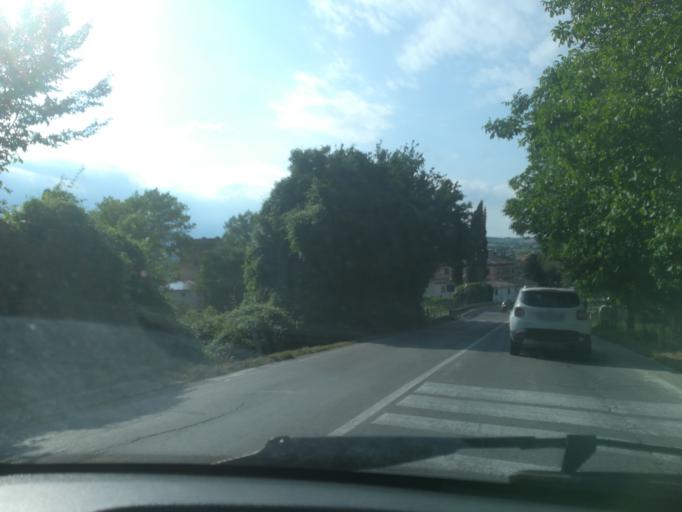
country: IT
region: The Marches
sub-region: Provincia di Macerata
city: Villa Potenza
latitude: 43.3191
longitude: 13.4280
